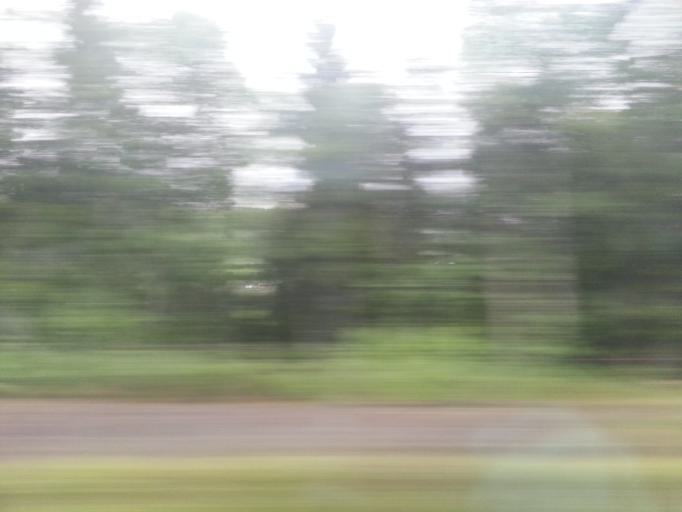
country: NO
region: Sor-Trondelag
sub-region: Midtre Gauldal
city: Storen
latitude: 62.9426
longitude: 10.1834
